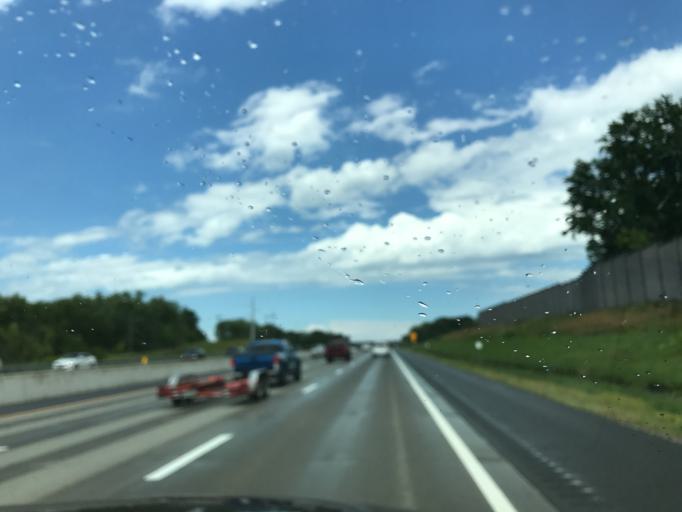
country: US
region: New York
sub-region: Albany County
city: Delmar
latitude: 42.6541
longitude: -73.8194
